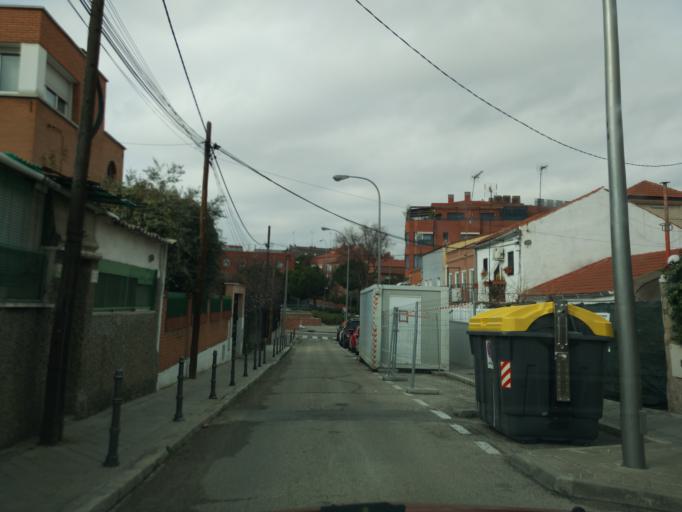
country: ES
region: Madrid
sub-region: Provincia de Madrid
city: Hortaleza
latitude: 40.4665
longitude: -3.6502
